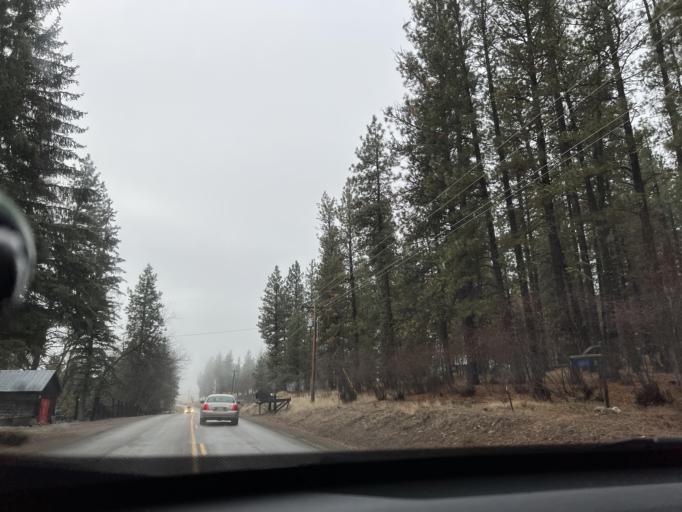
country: US
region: Washington
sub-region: Okanogan County
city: Brewster
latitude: 48.4652
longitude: -120.2077
